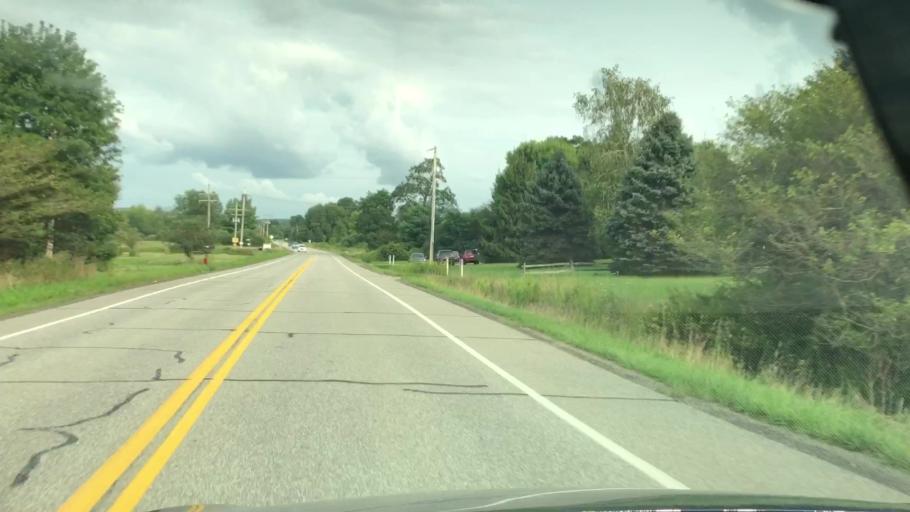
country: US
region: Pennsylvania
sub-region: Erie County
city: Northwest Harborcreek
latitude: 42.0592
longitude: -79.8657
